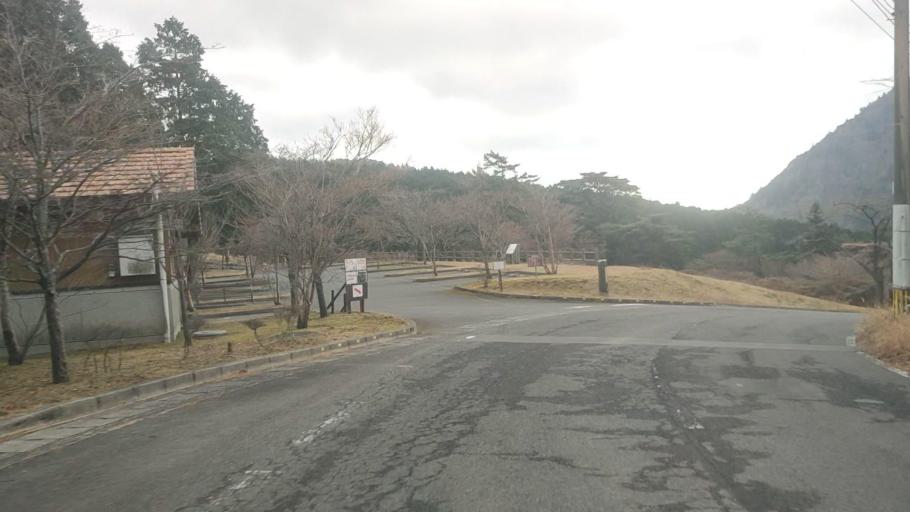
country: JP
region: Nagasaki
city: Shimabara
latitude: 32.7488
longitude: 130.2744
